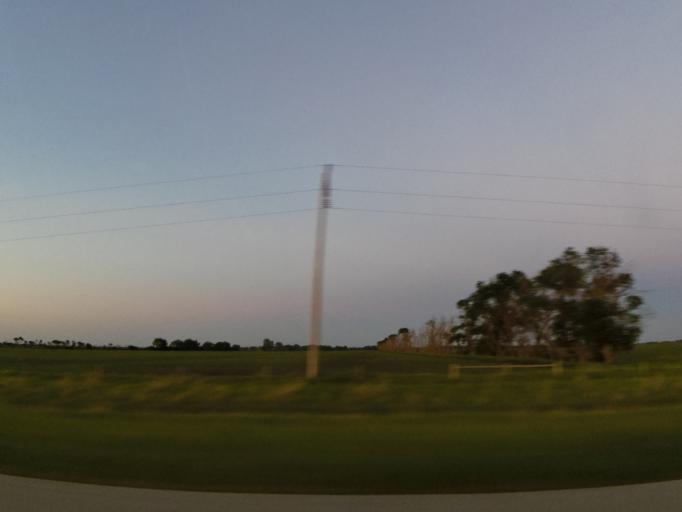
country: US
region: North Dakota
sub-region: Walsh County
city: Grafton
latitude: 48.3904
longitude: -97.1901
